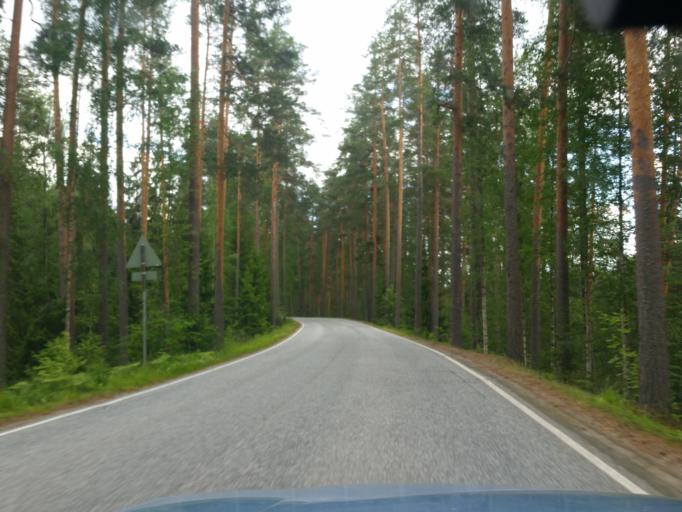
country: FI
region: Southern Savonia
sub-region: Savonlinna
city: Sulkava
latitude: 61.7912
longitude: 28.4236
